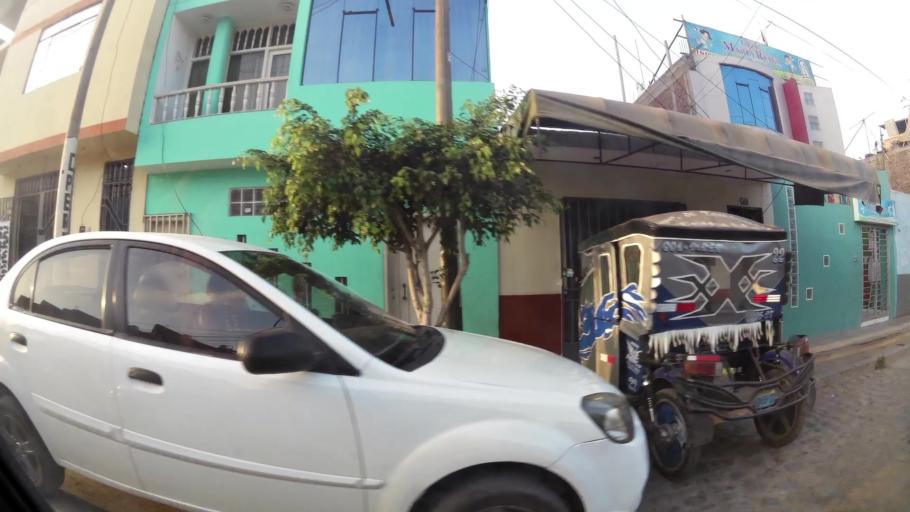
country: PE
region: La Libertad
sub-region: Provincia de Trujillo
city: El Porvenir
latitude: -8.0810
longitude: -79.0010
